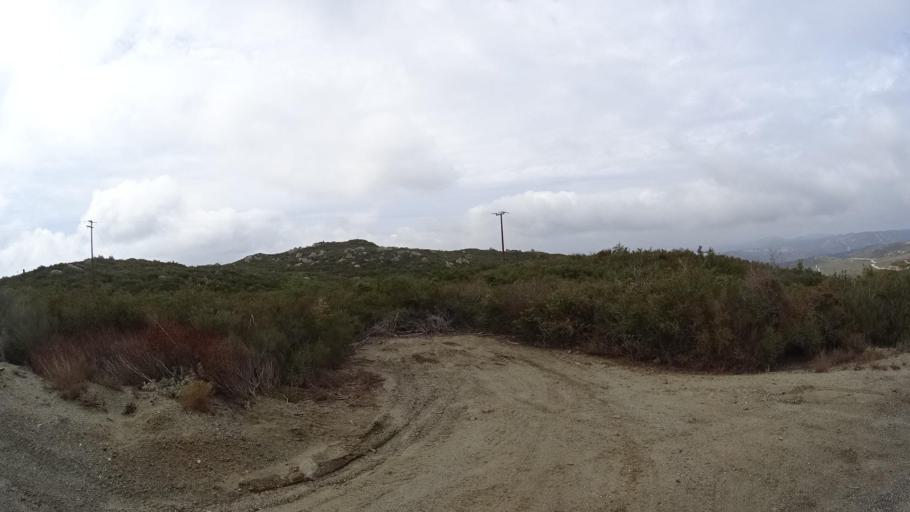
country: US
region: California
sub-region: San Diego County
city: Descanso
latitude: 32.9325
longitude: -116.6381
